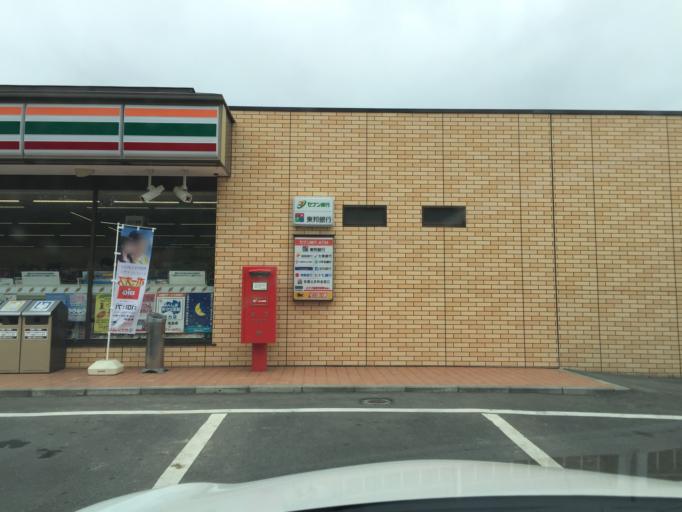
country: JP
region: Fukushima
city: Funehikimachi-funehiki
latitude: 37.3986
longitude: 140.6220
